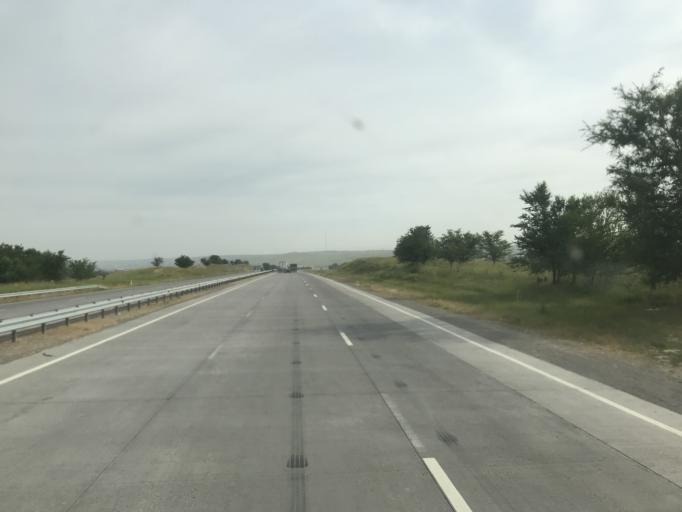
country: KZ
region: Ongtustik Qazaqstan
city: Shymkent
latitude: 42.1958
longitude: 69.5076
